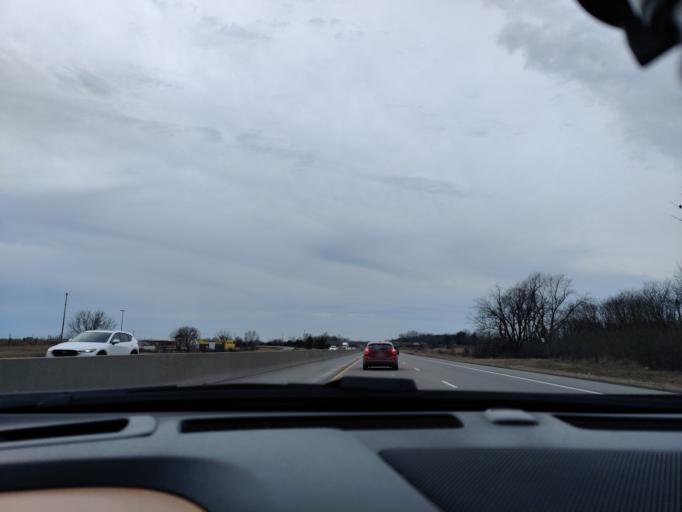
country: CA
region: Ontario
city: Belleville
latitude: 44.1812
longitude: -77.4415
